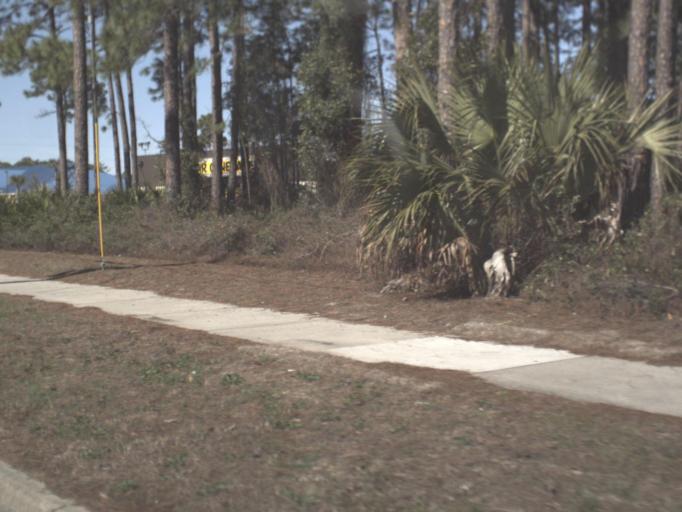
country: US
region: Florida
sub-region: Bay County
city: Panama City Beach
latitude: 30.1959
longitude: -85.8294
